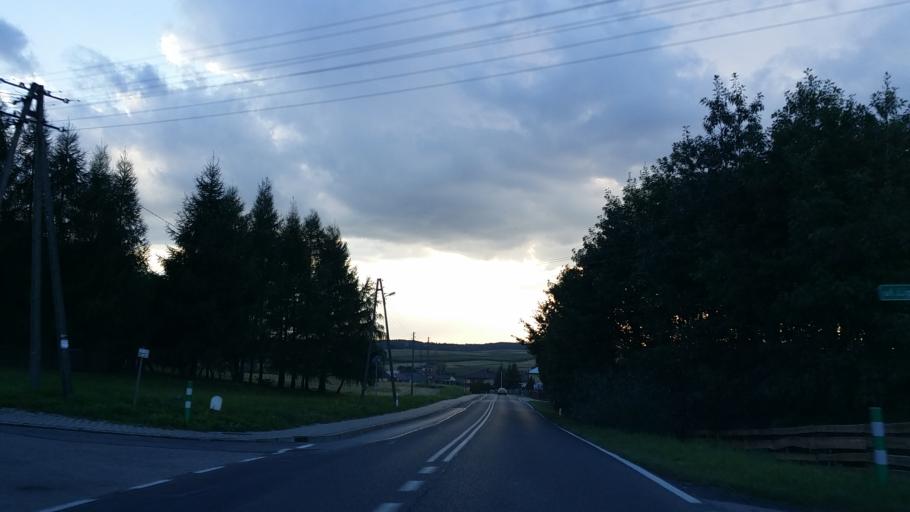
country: PL
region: Lesser Poland Voivodeship
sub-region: Powiat oswiecimski
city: Polanka Wielka
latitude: 49.9802
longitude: 19.3042
